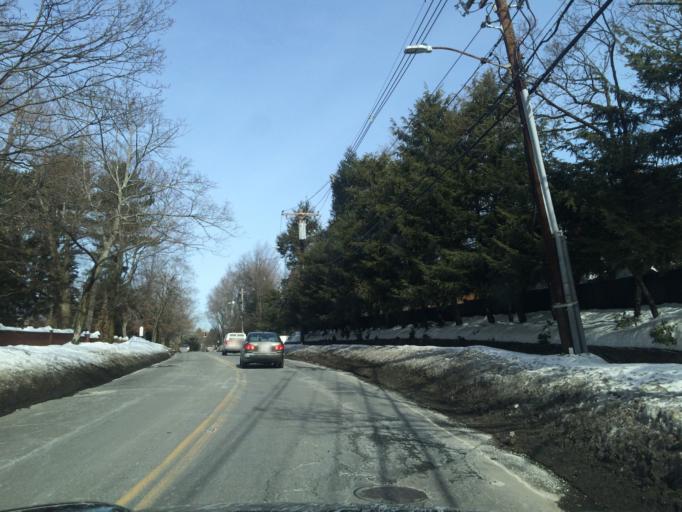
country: US
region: Massachusetts
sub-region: Norfolk County
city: Brookline
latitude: 42.3315
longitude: -71.1462
